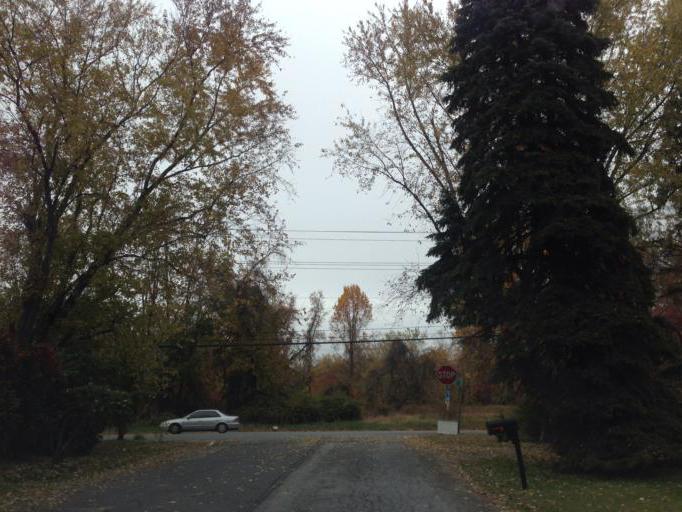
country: US
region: Maryland
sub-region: Howard County
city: Ellicott City
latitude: 39.3023
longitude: -76.8262
